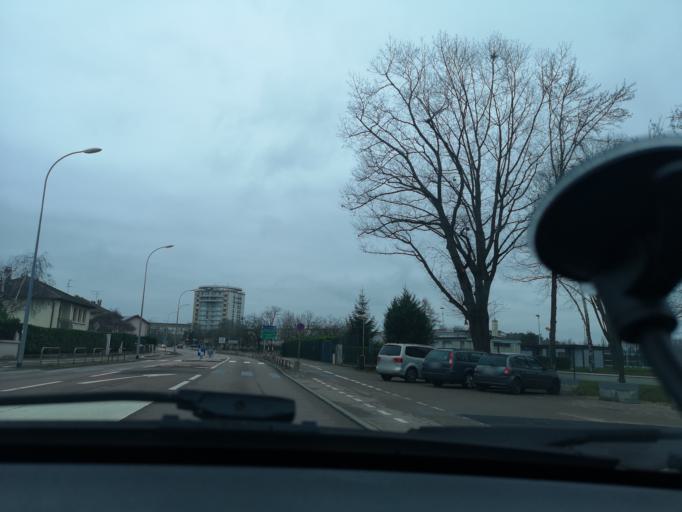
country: FR
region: Bourgogne
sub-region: Departement de Saone-et-Loire
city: Champforgeuil
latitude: 46.8072
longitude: 4.8472
